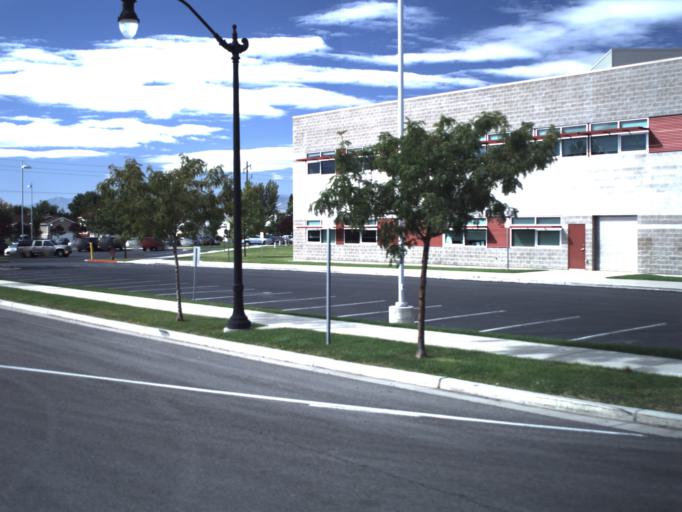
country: US
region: Utah
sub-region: Davis County
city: North Salt Lake
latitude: 40.8071
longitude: -111.9392
